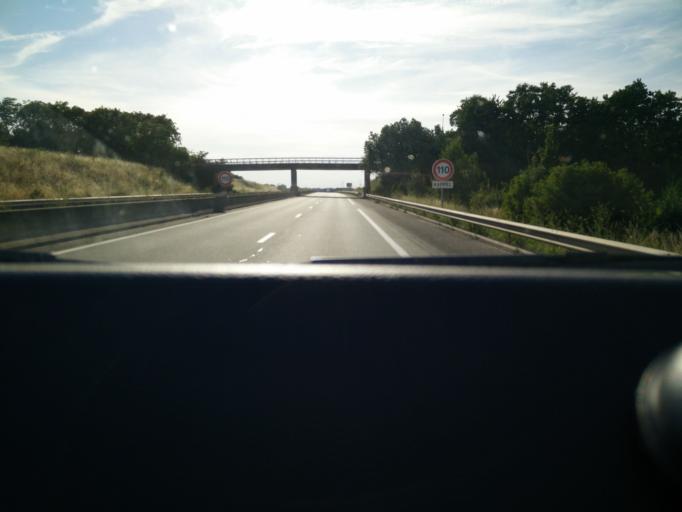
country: FR
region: Nord-Pas-de-Calais
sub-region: Departement du Nord
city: Abscon
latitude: 50.3455
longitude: 3.2972
